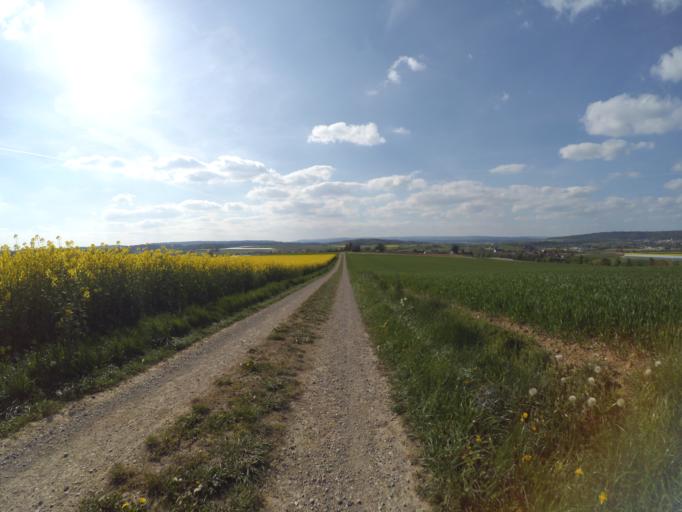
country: CH
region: Thurgau
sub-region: Frauenfeld District
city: Diessenhofen
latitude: 47.6628
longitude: 8.7580
